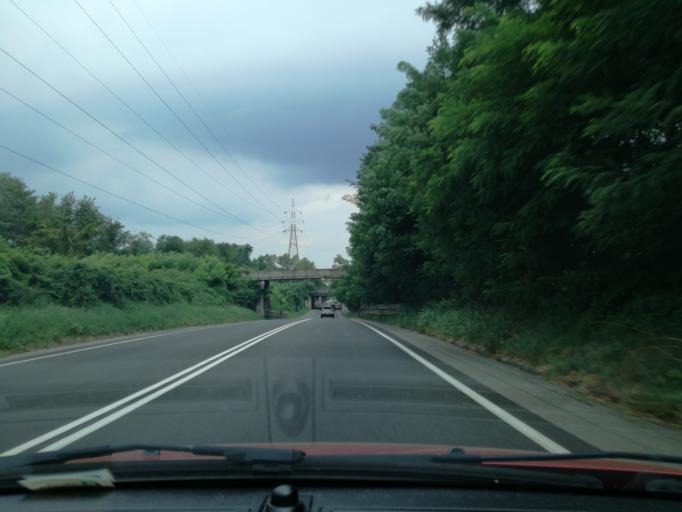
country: IT
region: Lombardy
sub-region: Provincia di Monza e Brianza
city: Velasca
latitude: 45.6390
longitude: 9.3537
